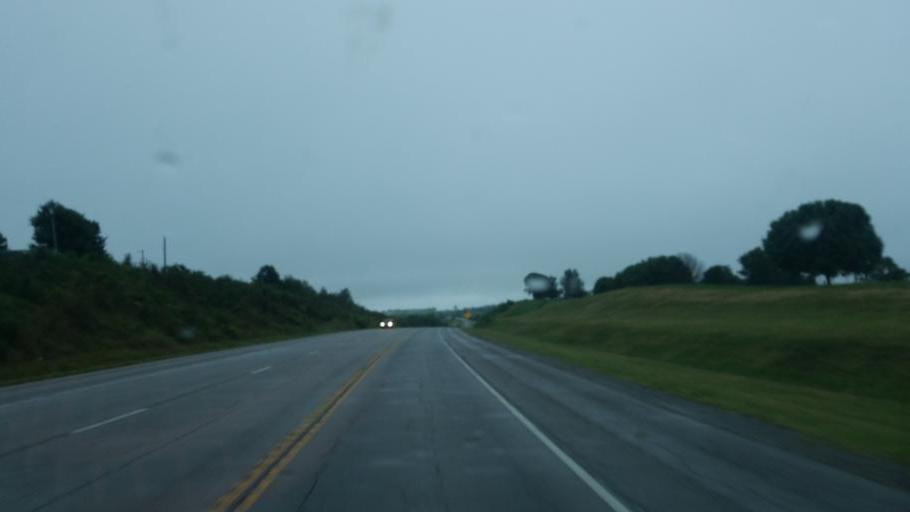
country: US
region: Kentucky
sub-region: Fleming County
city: Flemingsburg
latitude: 38.4074
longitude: -83.7304
